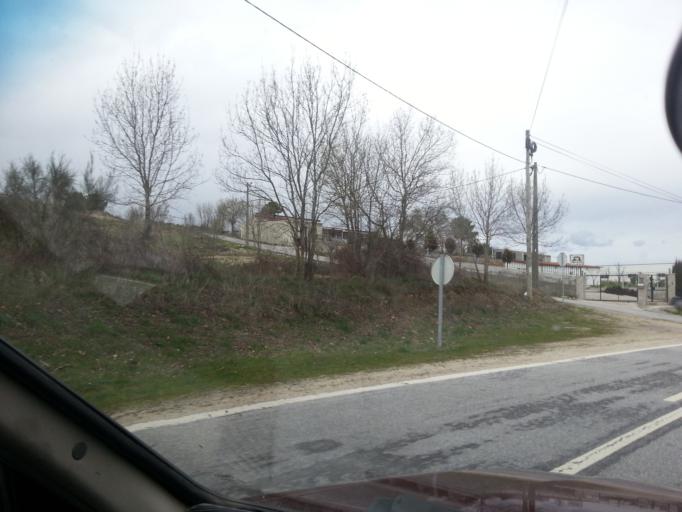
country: PT
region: Guarda
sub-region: Fornos de Algodres
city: Fornos de Algodres
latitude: 40.5666
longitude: -7.4722
